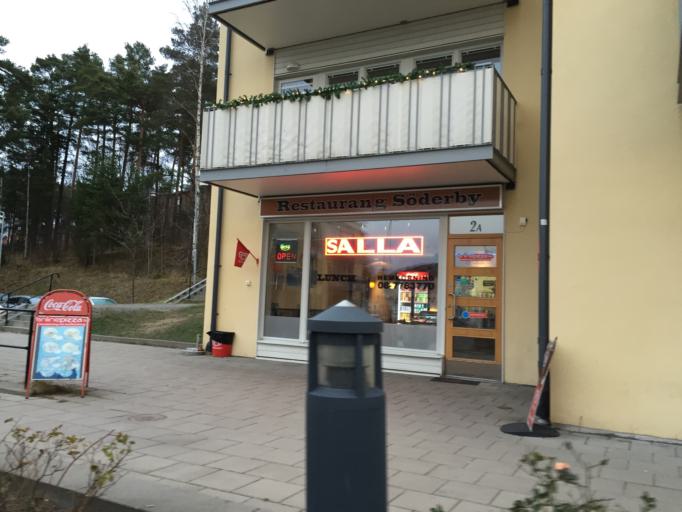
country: SE
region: Stockholm
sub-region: Botkyrka Kommun
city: Varsta
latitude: 59.2031
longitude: 17.7874
